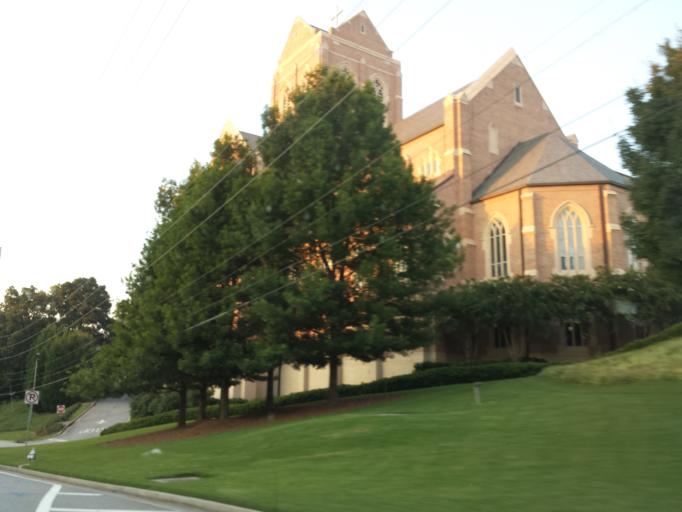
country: US
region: Georgia
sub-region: Cobb County
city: Vinings
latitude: 33.8520
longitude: -84.4305
